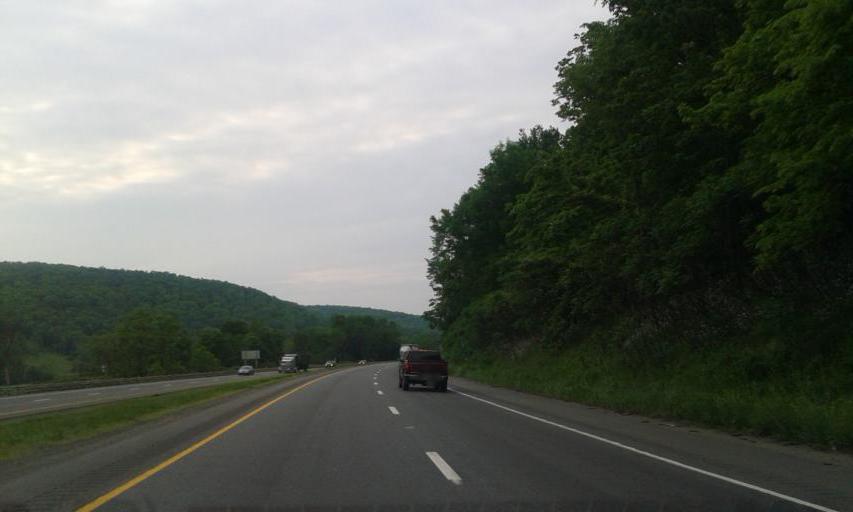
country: US
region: Pennsylvania
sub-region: Wyoming County
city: Factoryville
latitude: 41.7176
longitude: -75.6739
